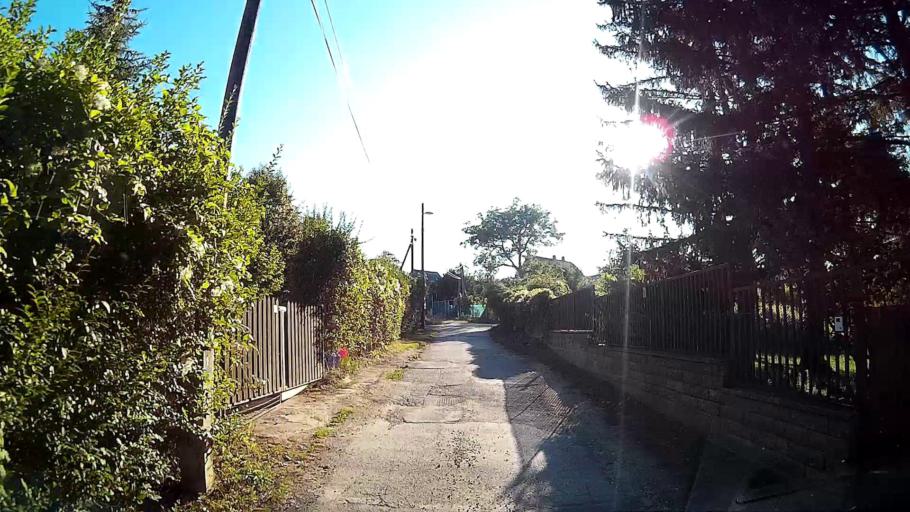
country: HU
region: Pest
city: Csobanka
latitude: 47.6429
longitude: 18.9594
